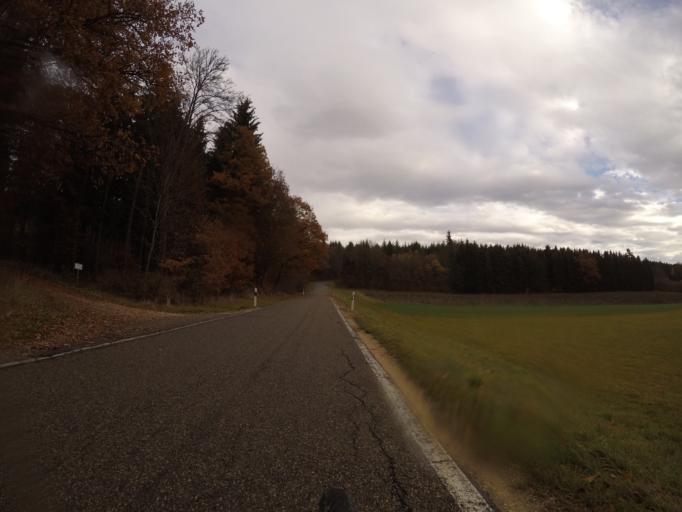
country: DE
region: Baden-Wuerttemberg
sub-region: Tuebingen Region
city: Sankt Johann
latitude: 48.4086
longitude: 9.3035
